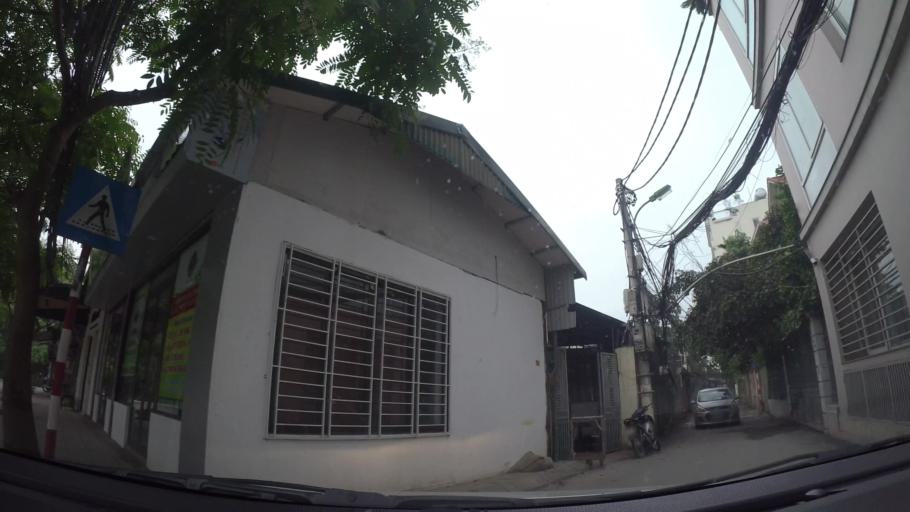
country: VN
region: Ha Noi
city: Tay Ho
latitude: 21.0621
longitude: 105.8210
